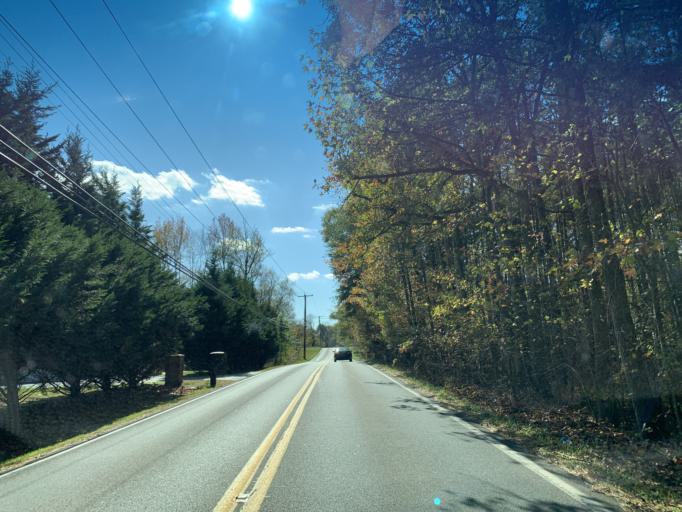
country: US
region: Maryland
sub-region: Anne Arundel County
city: Gambrills
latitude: 39.0951
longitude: -76.6534
